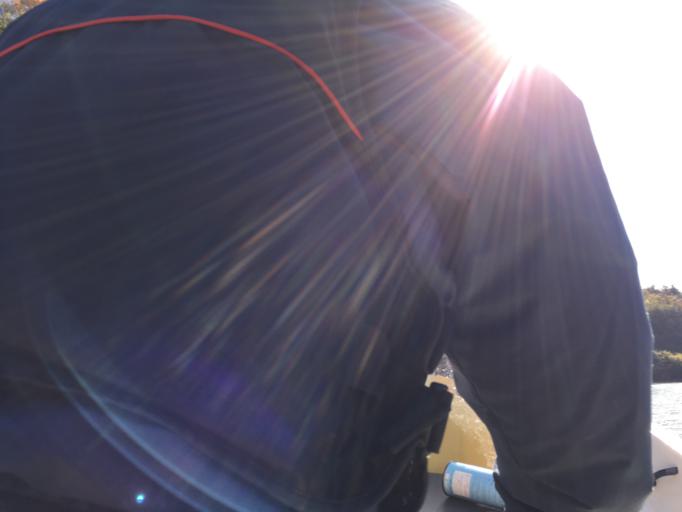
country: JP
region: Iwate
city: Ichinoseki
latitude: 38.8007
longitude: 141.2899
